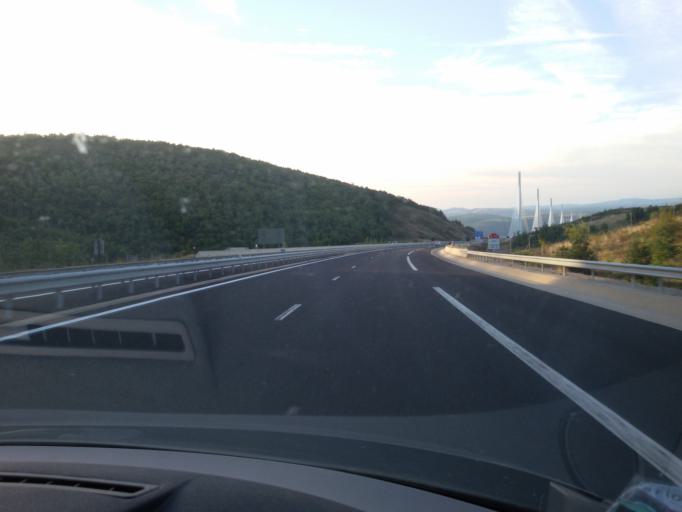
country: FR
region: Midi-Pyrenees
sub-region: Departement de l'Aveyron
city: Creissels
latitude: 44.0631
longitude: 3.0268
